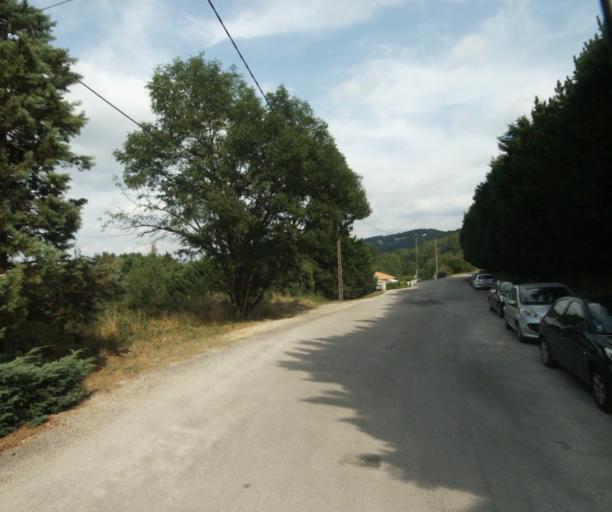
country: FR
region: Midi-Pyrenees
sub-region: Departement de la Haute-Garonne
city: Revel
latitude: 43.4410
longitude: 2.0337
